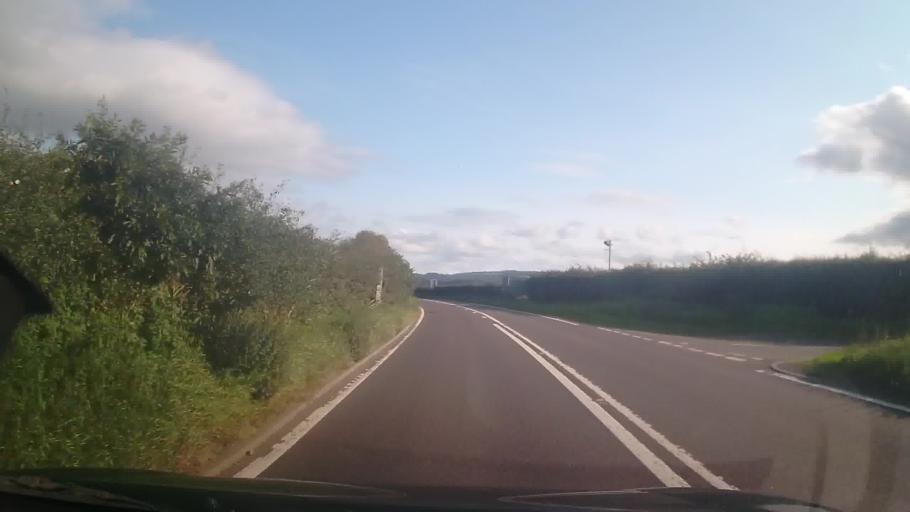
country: GB
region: England
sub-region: Shropshire
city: Bromfield
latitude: 52.4045
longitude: -2.8040
